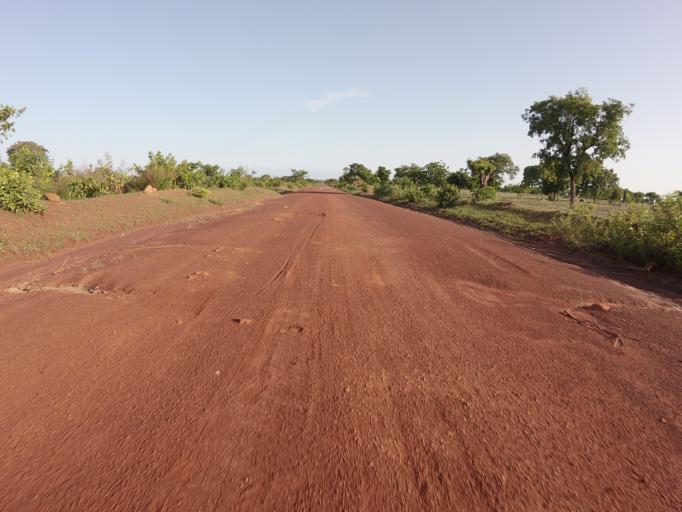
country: TG
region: Savanes
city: Sansanne-Mango
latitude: 10.3793
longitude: -0.0946
